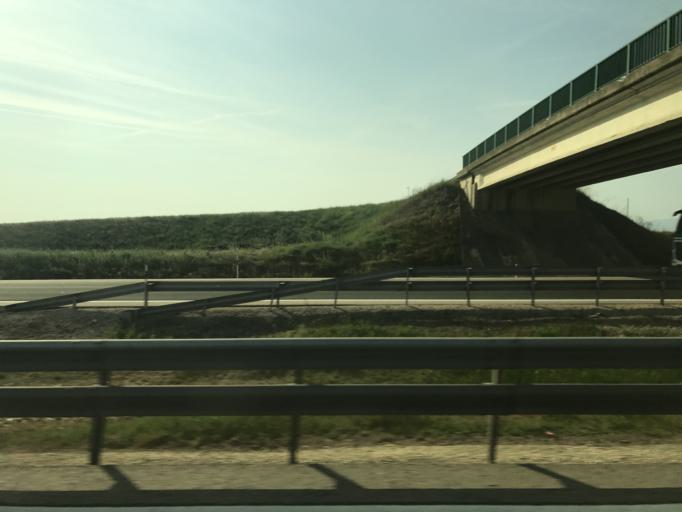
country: ES
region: Castille and Leon
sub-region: Provincia de Burgos
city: Grisalena
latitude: 42.5656
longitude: -3.2658
